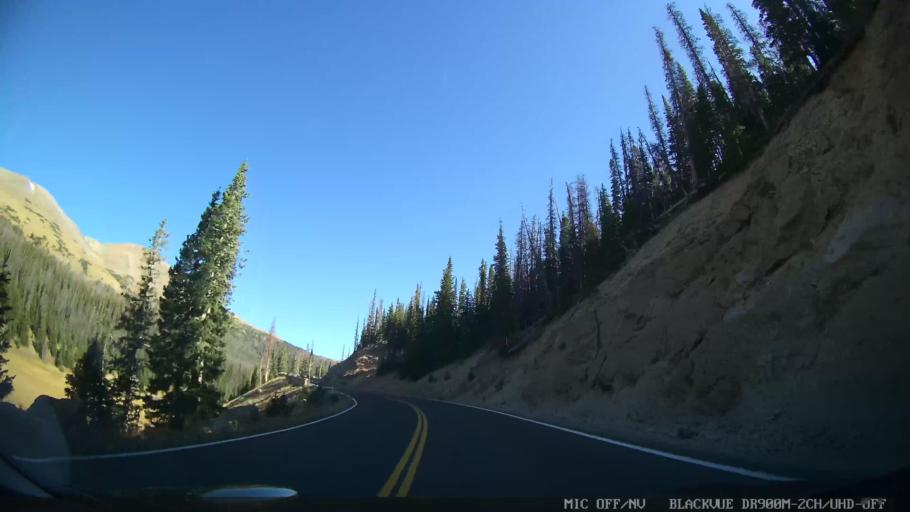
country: US
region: Colorado
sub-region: Larimer County
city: Estes Park
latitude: 40.4265
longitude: -105.8039
